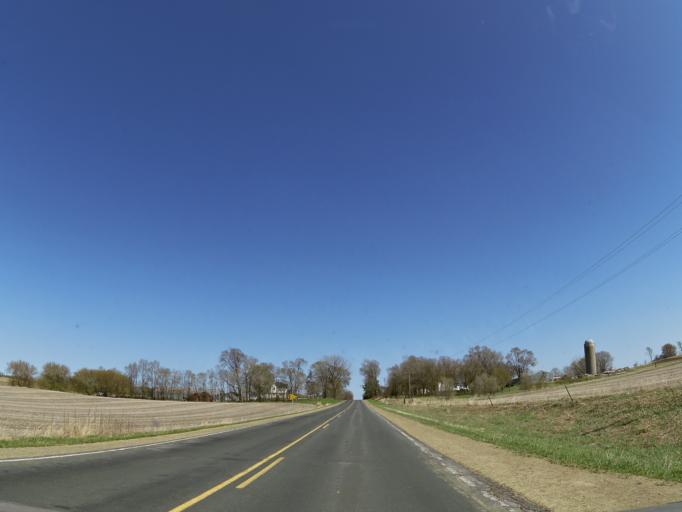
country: US
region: Wisconsin
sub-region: Saint Croix County
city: Roberts
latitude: 44.9351
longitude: -92.5109
